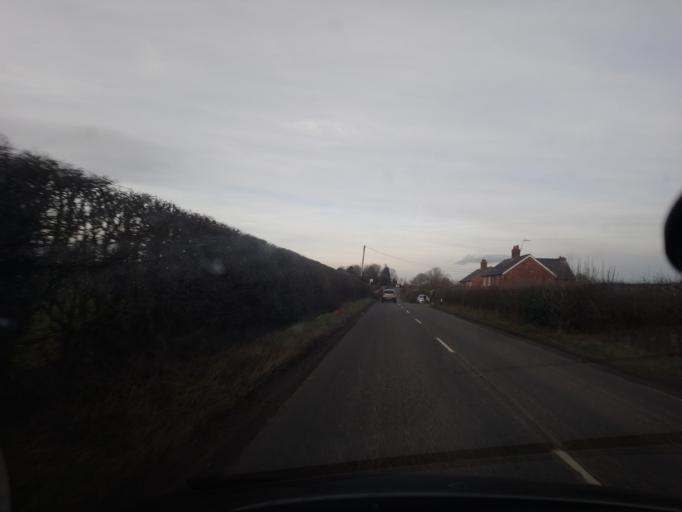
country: GB
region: England
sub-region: Shropshire
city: Wem
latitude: 52.8986
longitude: -2.7073
